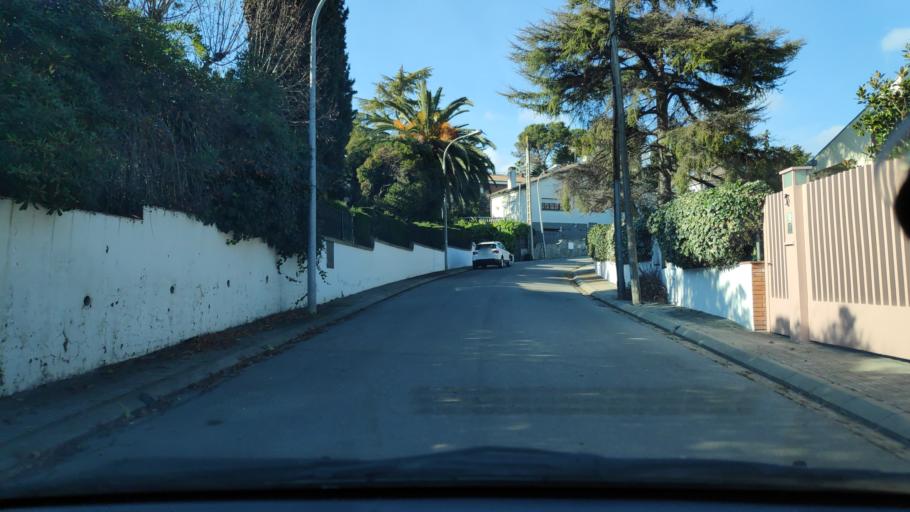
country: ES
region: Catalonia
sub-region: Provincia de Barcelona
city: Sant Quirze del Valles
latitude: 41.5057
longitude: 2.0908
